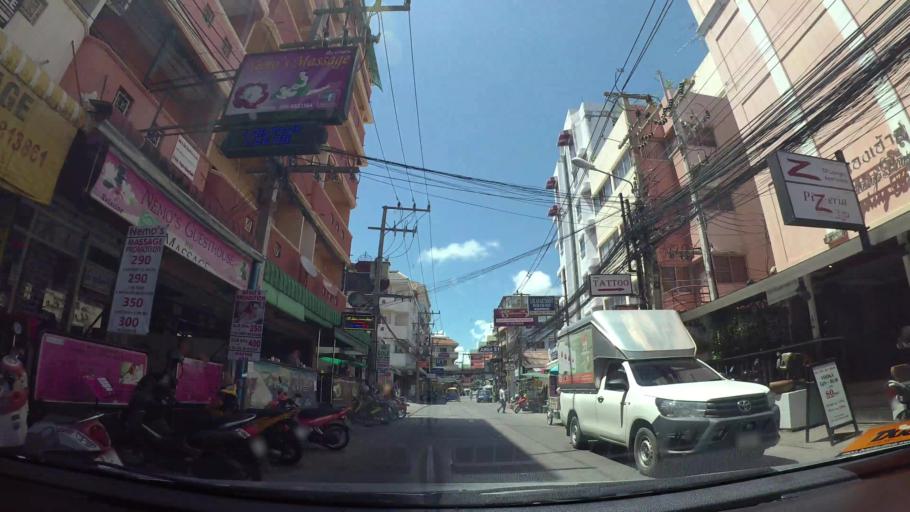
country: TH
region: Chon Buri
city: Phatthaya
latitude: 12.9293
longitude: 100.8841
